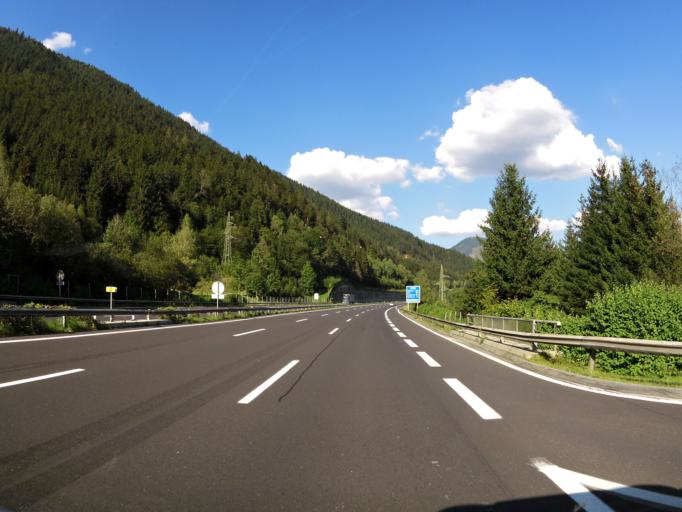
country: AT
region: Styria
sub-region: Politischer Bezirk Liezen
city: Ardning
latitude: 47.5803
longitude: 14.3218
